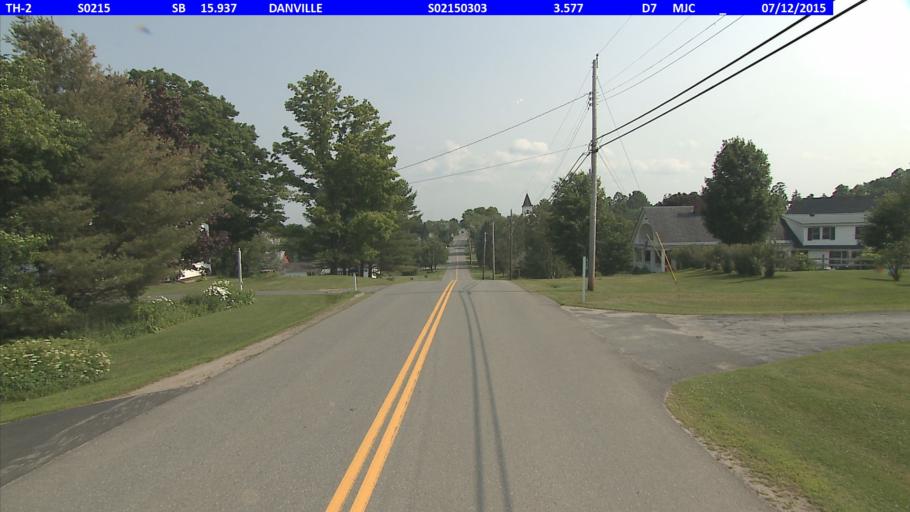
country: US
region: Vermont
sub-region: Caledonia County
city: Saint Johnsbury
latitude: 44.4159
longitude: -72.1416
